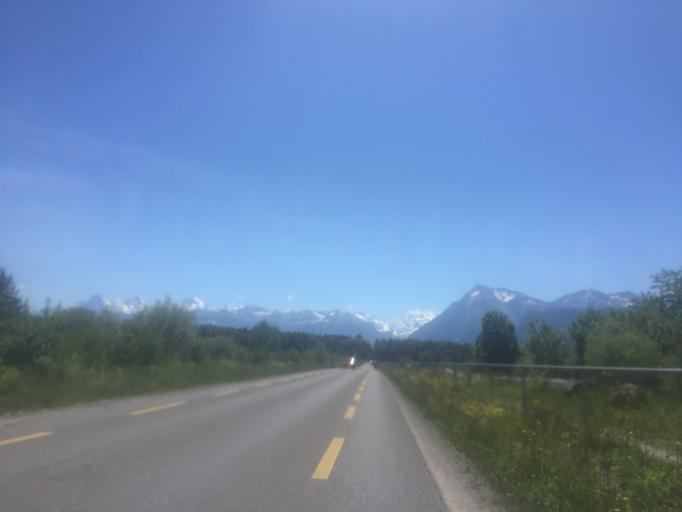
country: CH
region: Bern
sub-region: Thun District
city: Thierachern
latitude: 46.7510
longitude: 7.5887
